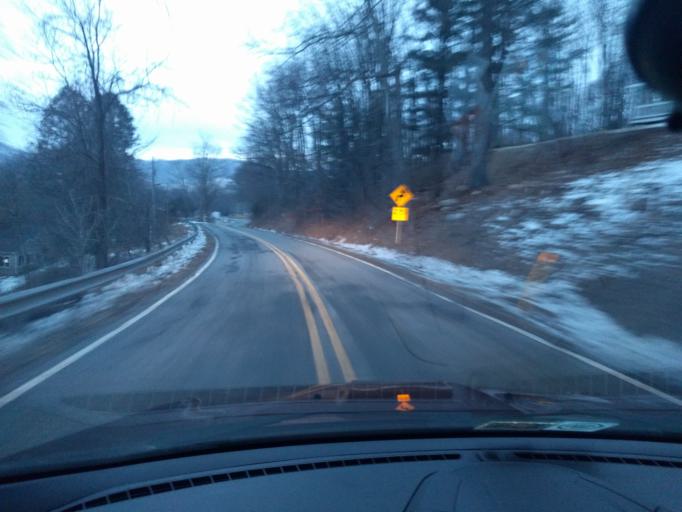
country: US
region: Virginia
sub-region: Alleghany County
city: Clifton Forge
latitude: 37.8934
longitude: -79.8874
